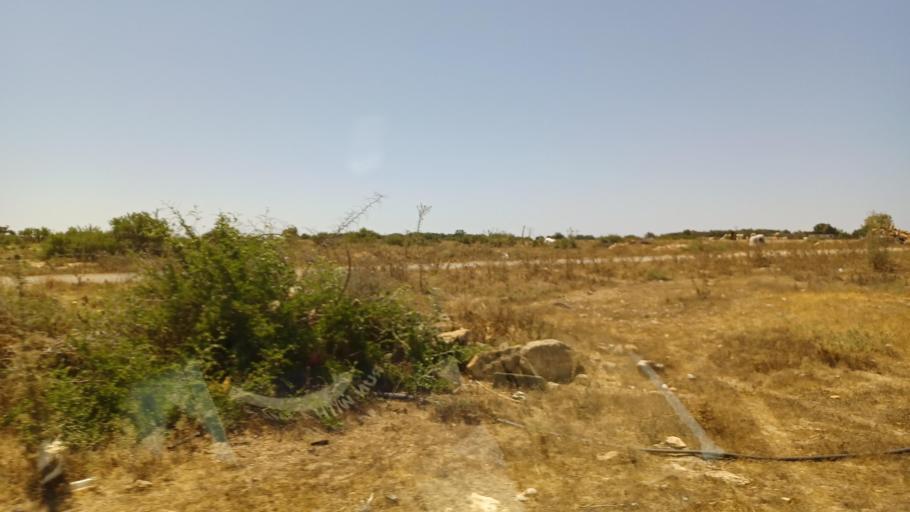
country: CY
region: Ammochostos
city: Avgorou
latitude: 35.0607
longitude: 33.8506
